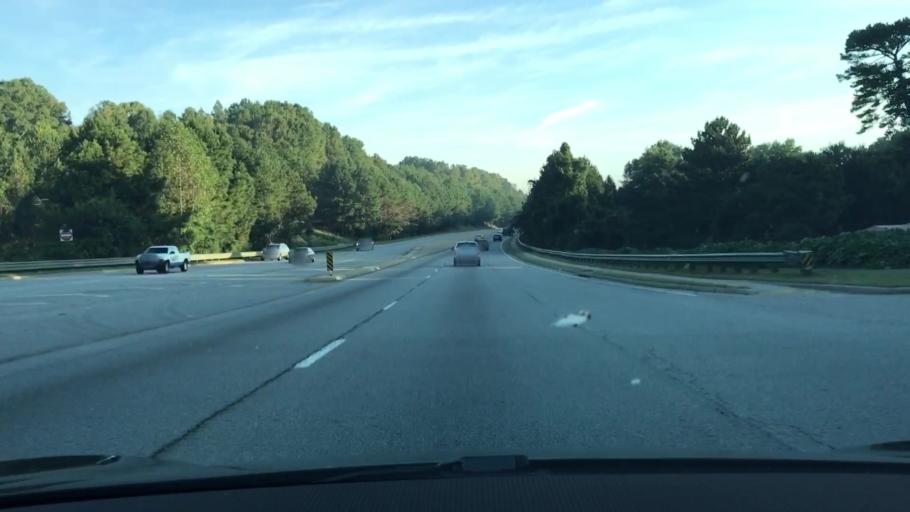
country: US
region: Georgia
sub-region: Gwinnett County
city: Sugar Hill
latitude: 34.1093
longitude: -84.0289
